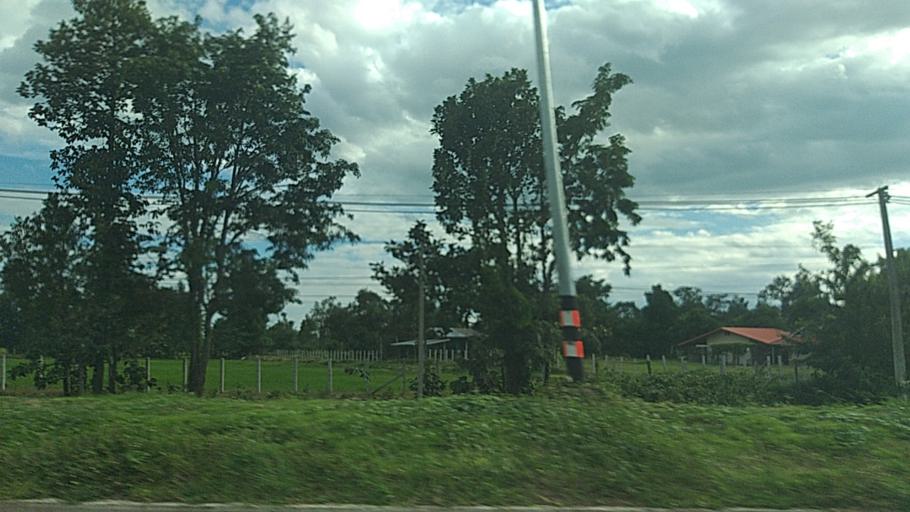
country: TH
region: Surin
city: Prasat
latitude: 14.5780
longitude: 103.4800
